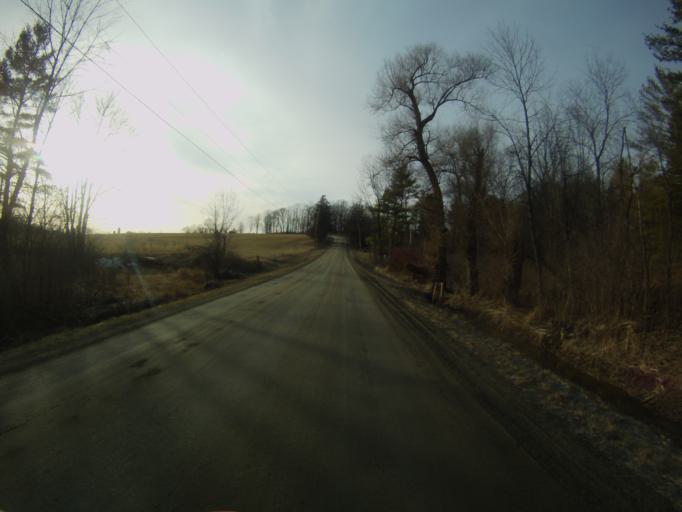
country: US
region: Vermont
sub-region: Addison County
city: Middlebury (village)
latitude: 44.0395
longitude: -73.2784
